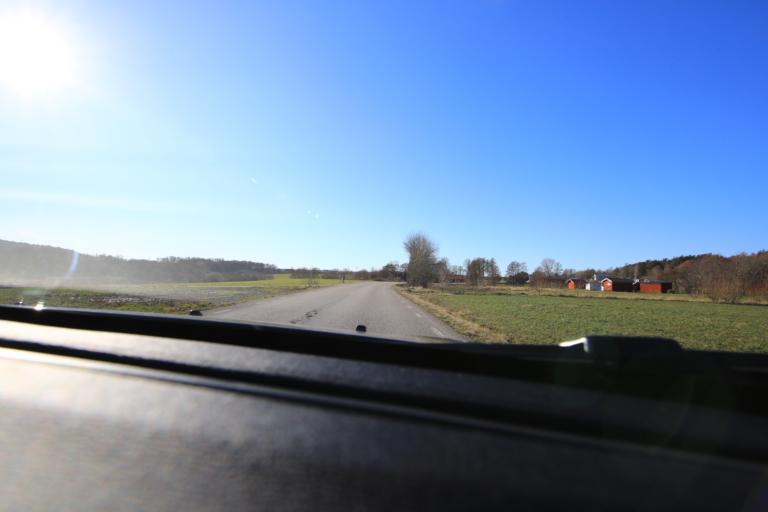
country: SE
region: Halland
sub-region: Varbergs Kommun
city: Tvaaker
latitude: 57.0590
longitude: 12.4364
